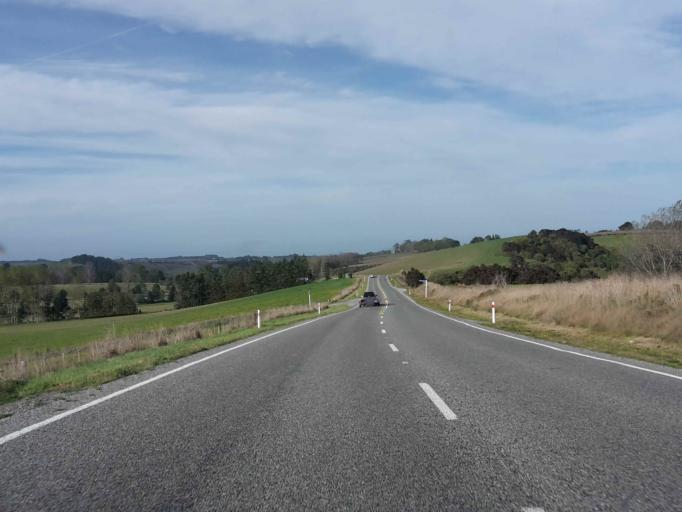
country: NZ
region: Canterbury
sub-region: Timaru District
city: Pleasant Point
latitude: -44.1201
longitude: 171.1175
